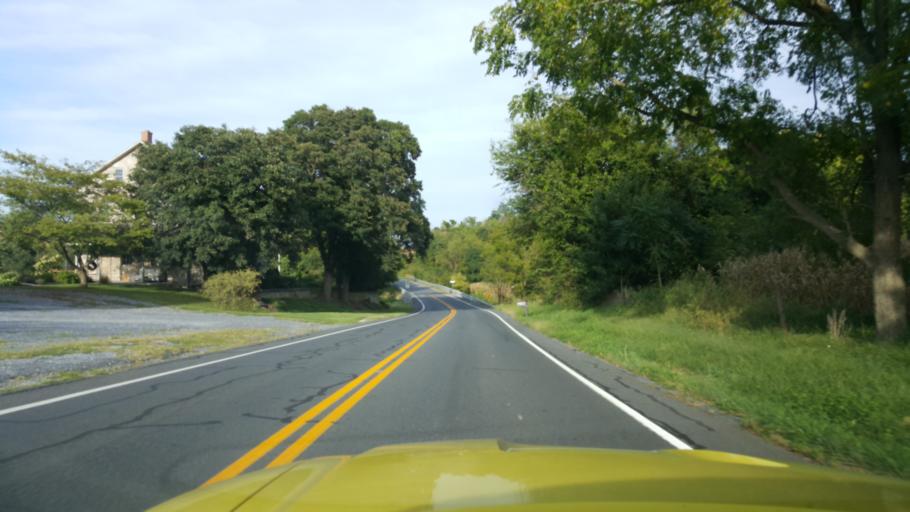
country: US
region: Pennsylvania
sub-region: Lebanon County
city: Palmyra
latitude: 40.3114
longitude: -76.5541
